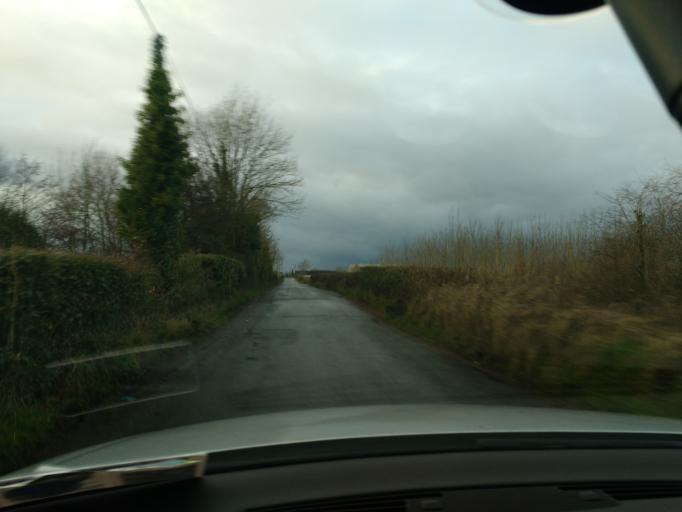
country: IE
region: Munster
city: Thurles
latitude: 52.6356
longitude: -7.8345
